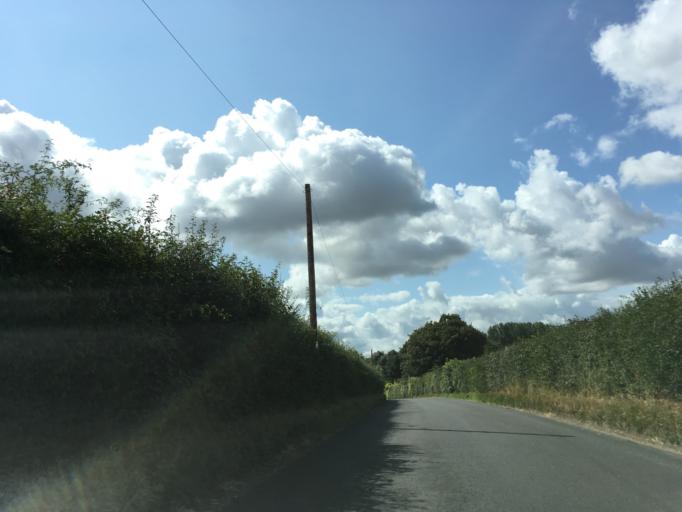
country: GB
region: England
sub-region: Hampshire
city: Kings Worthy
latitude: 51.1772
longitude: -1.3749
